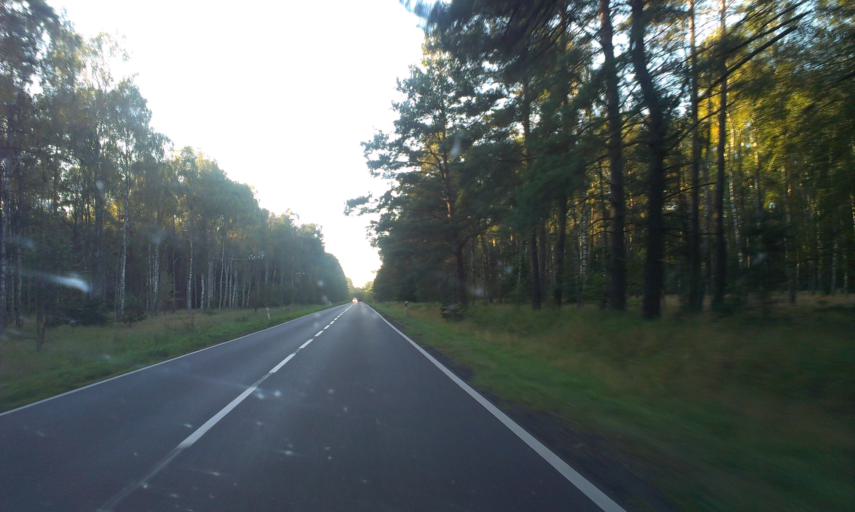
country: PL
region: Pomeranian Voivodeship
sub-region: Powiat czluchowski
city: Czarne
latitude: 53.7175
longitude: 16.8454
